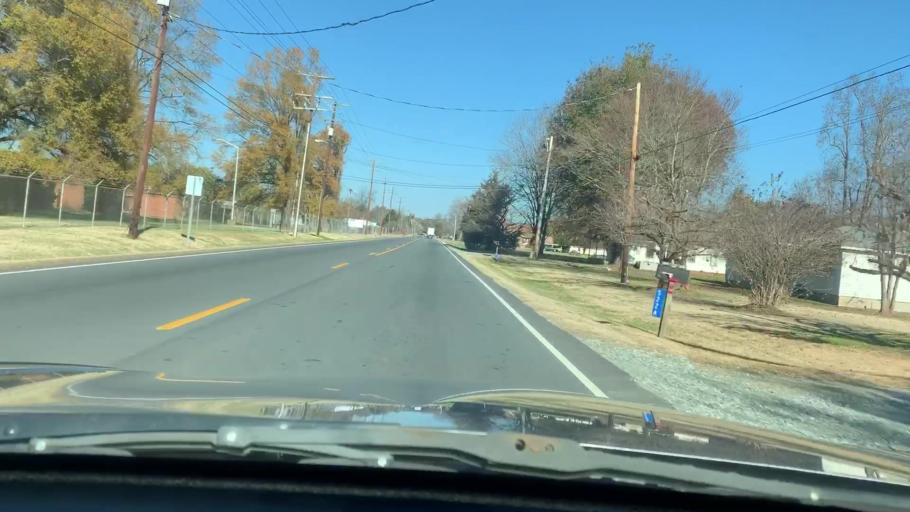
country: US
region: North Carolina
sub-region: Alamance County
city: Haw River
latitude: 36.0823
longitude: -79.3480
